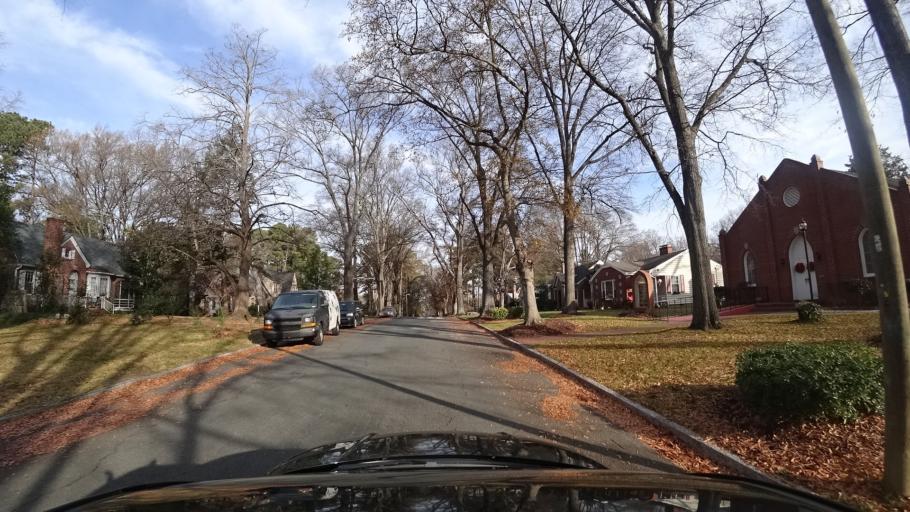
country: US
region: North Carolina
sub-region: Durham County
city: Durham
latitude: 36.0103
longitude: -78.8944
